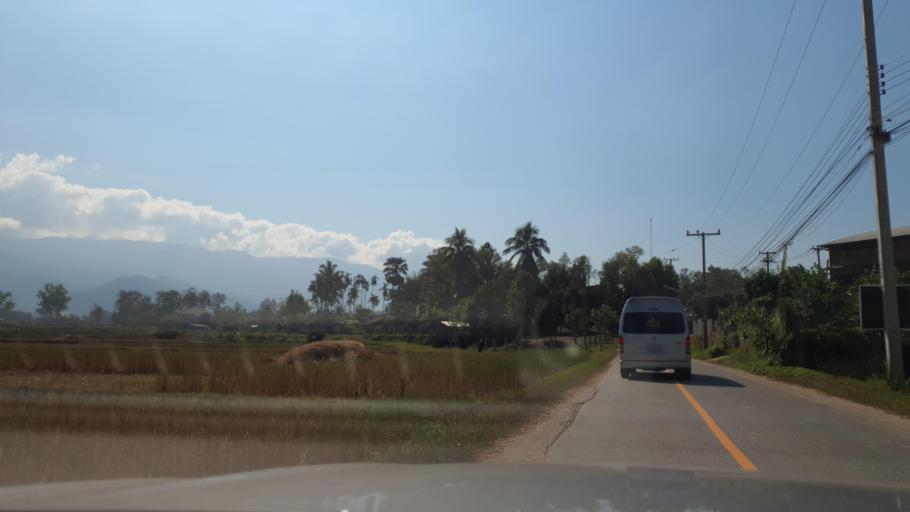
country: TH
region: Nan
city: Pua
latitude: 19.1627
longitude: 100.9292
